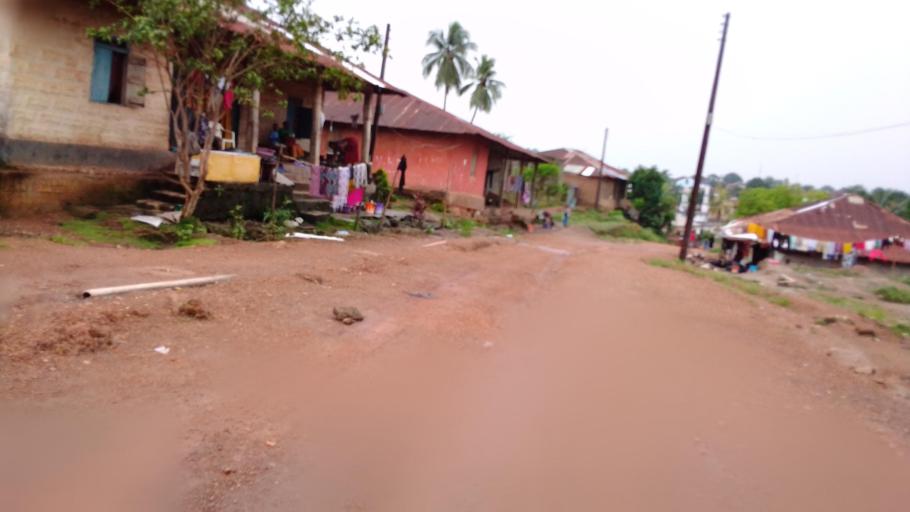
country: SL
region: Eastern Province
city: Kenema
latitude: 7.8693
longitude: -11.1922
